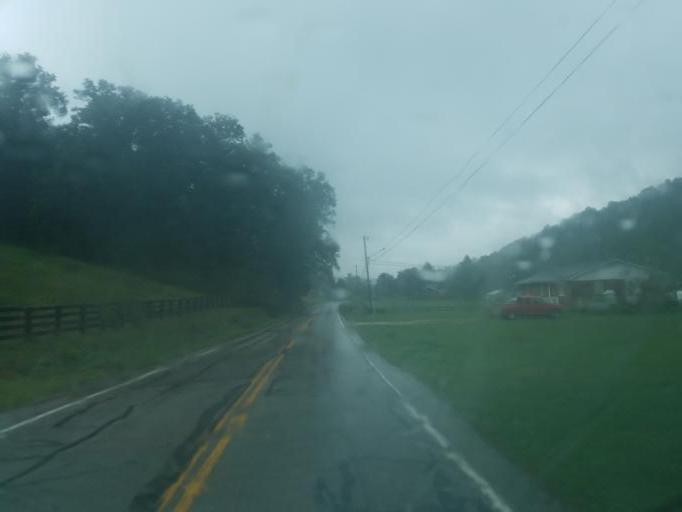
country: US
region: Kentucky
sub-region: Carter County
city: Olive Hill
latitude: 38.2883
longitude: -83.2954
